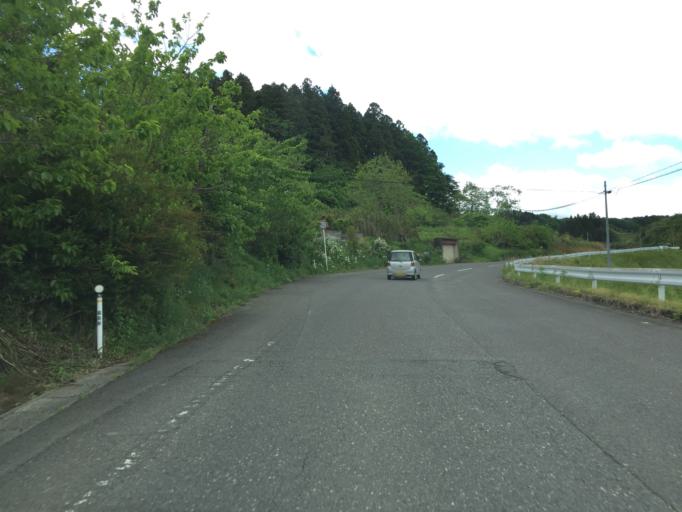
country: JP
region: Fukushima
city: Miharu
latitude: 37.4804
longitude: 140.4689
